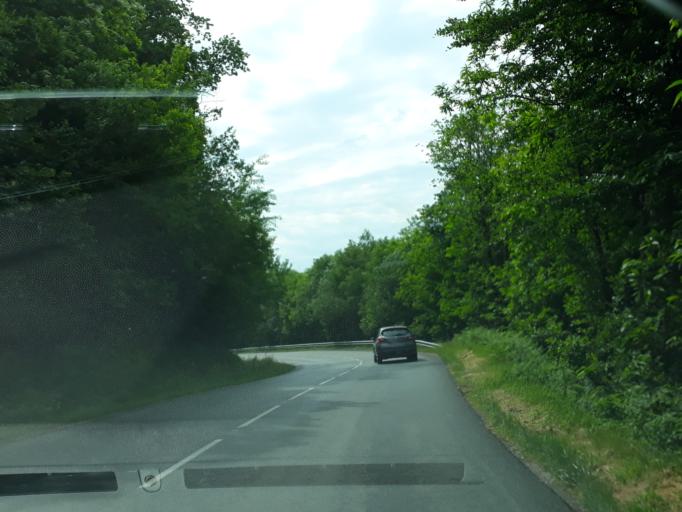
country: FR
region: Limousin
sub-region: Departement de la Correze
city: Beynat
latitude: 45.1288
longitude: 1.7402
